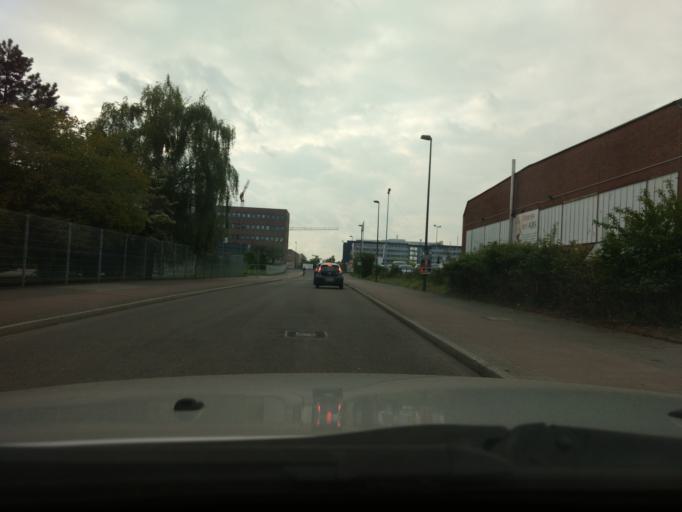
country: DE
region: North Rhine-Westphalia
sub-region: Regierungsbezirk Dusseldorf
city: Meerbusch
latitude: 51.2398
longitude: 6.7184
